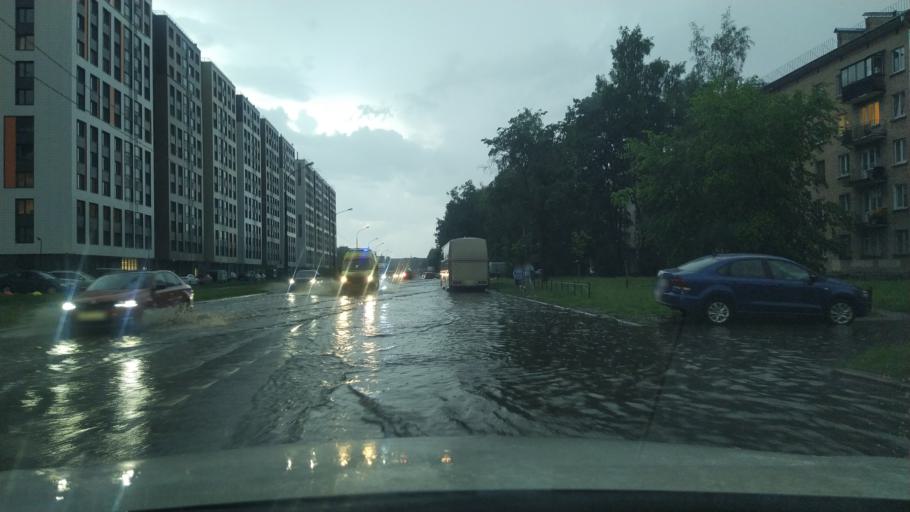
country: RU
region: Leningrad
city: Sampsonievskiy
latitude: 59.9845
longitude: 30.3526
